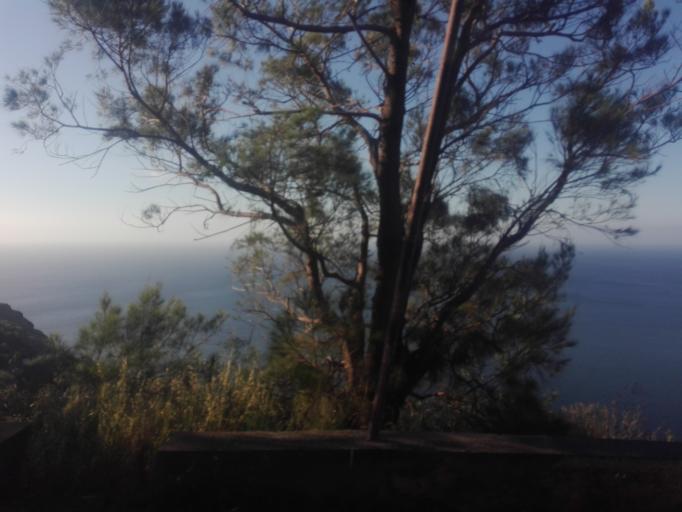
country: PT
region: Madeira
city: Canico
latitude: 32.6452
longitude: -16.8677
